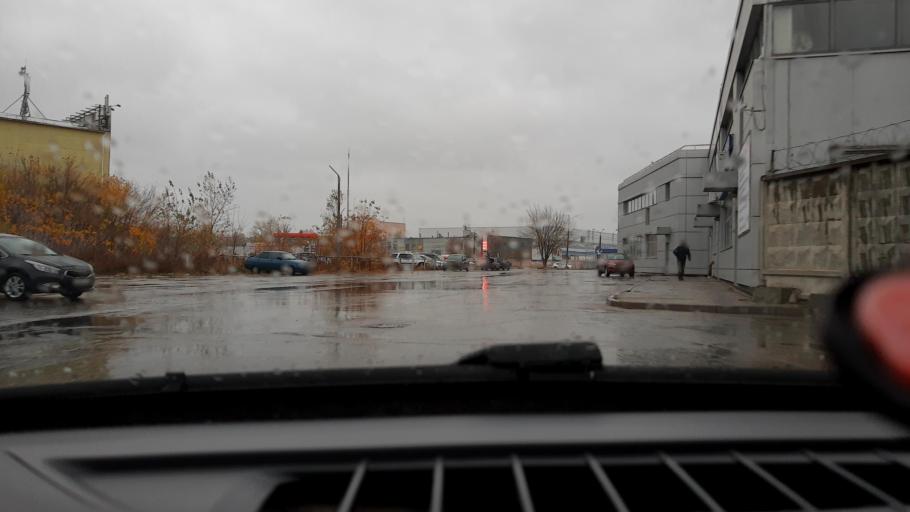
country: RU
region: Nizjnij Novgorod
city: Nizhniy Novgorod
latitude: 56.3094
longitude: 43.8979
